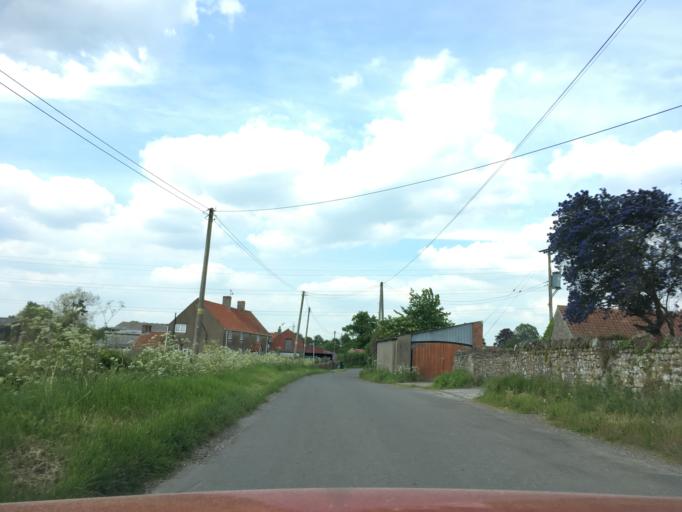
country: GB
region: England
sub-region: South Gloucestershire
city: Thornbury
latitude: 51.6236
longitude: -2.5184
